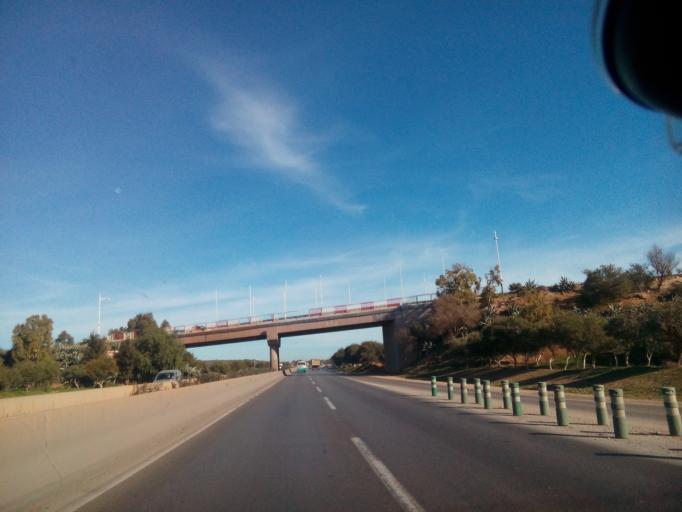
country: DZ
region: Oran
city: Ain el Bya
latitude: 35.7847
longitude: -0.4115
